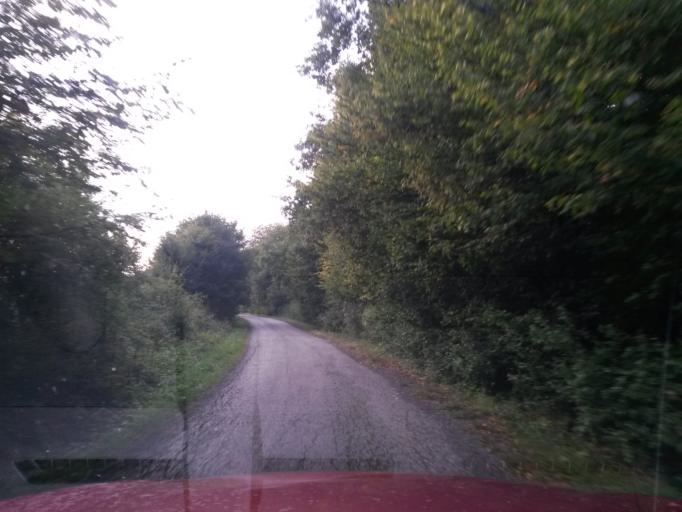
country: SK
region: Kosicky
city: Kosice
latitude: 48.7652
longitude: 21.4566
